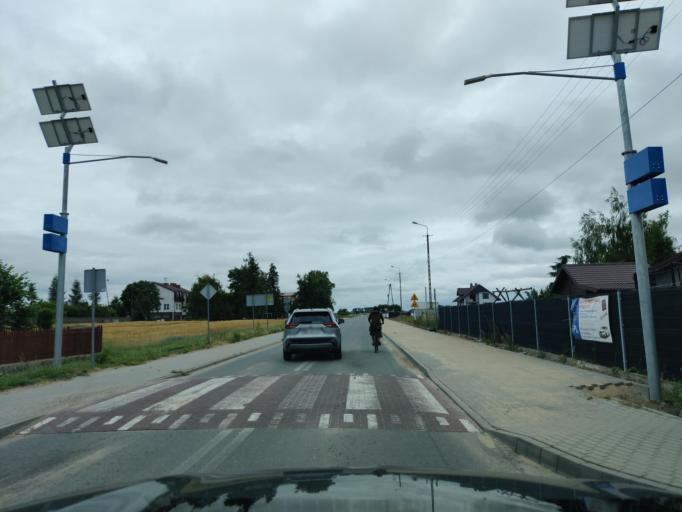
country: PL
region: Masovian Voivodeship
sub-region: Powiat przasnyski
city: Przasnysz
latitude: 52.9826
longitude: 20.9191
